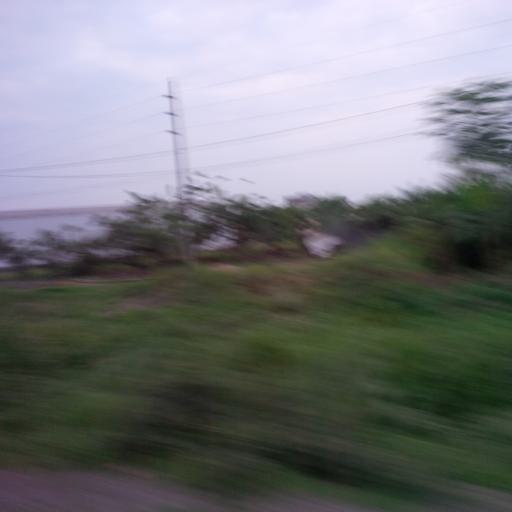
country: EC
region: Canar
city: La Troncal
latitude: -2.3382
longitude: -79.3892
